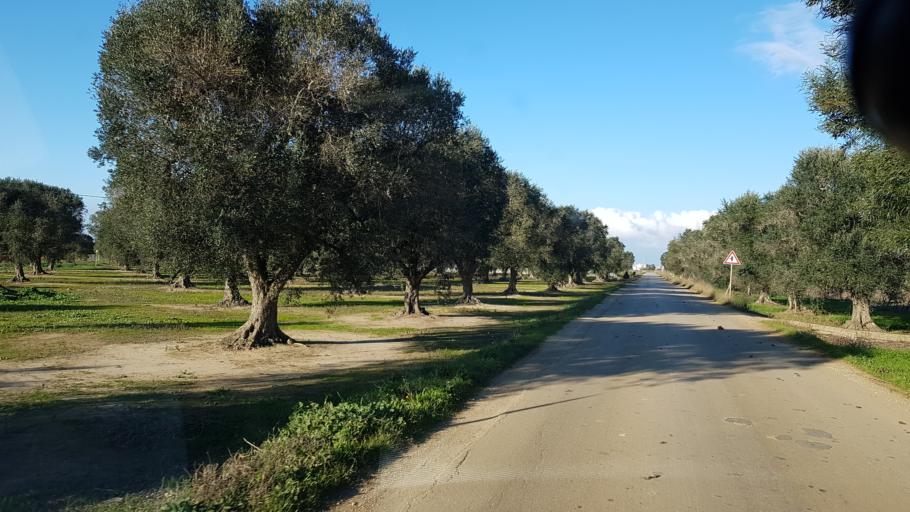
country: IT
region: Apulia
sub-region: Provincia di Brindisi
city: Tuturano
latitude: 40.5692
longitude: 17.8990
